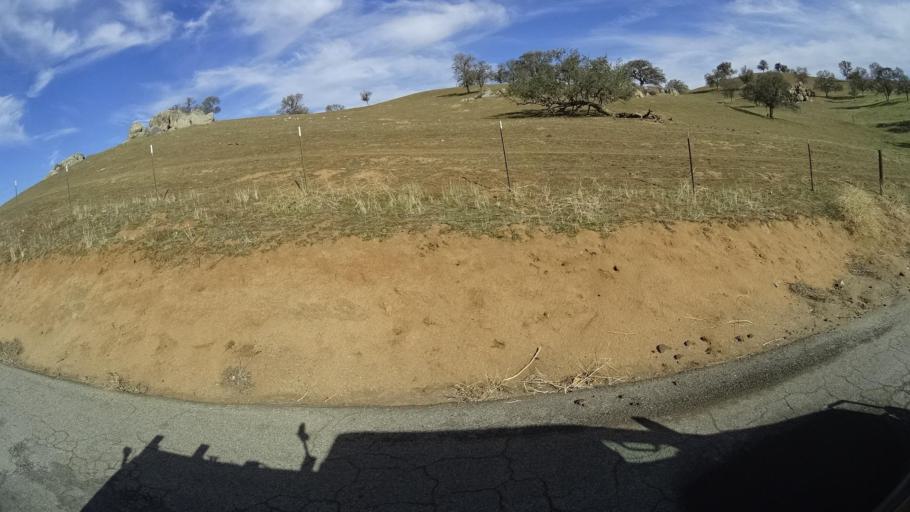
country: US
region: California
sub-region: Kern County
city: Oildale
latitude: 35.6148
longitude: -118.8465
